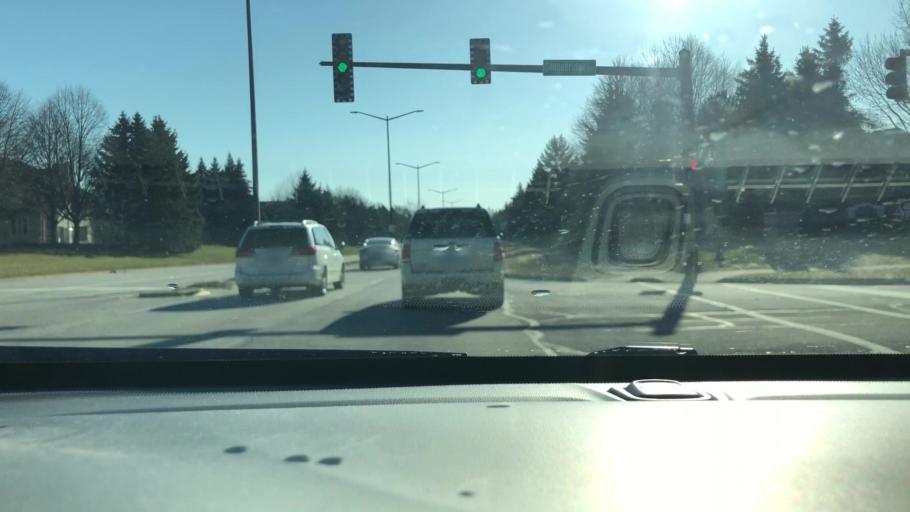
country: US
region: Illinois
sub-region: Kane County
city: Aurora
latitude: 41.7826
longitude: -88.2594
